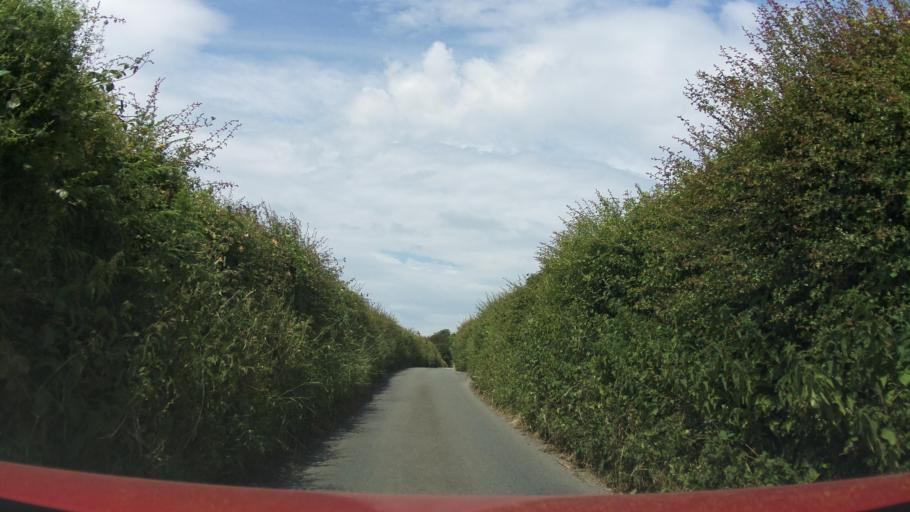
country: GB
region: Wales
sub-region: Vale of Glamorgan
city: Wick
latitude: 51.4311
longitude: -3.5622
